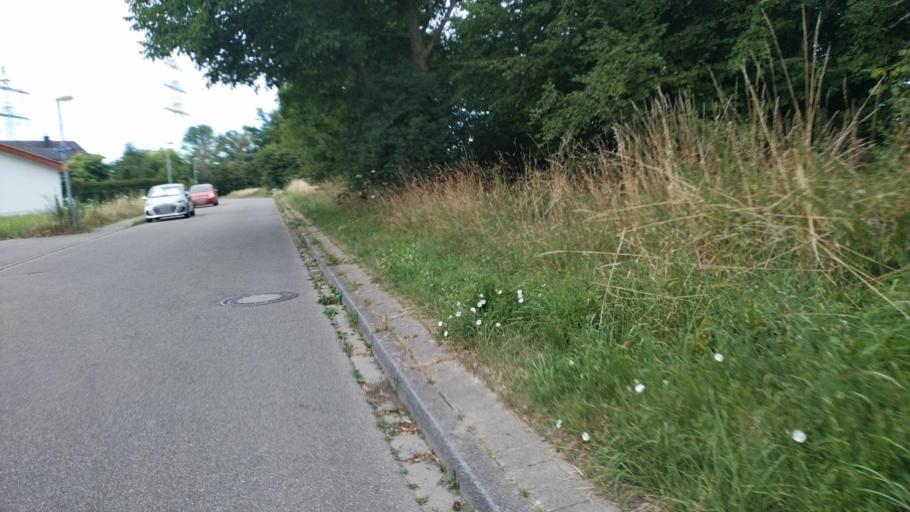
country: DE
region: Baden-Wuerttemberg
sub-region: Karlsruhe Region
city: Ettlingen
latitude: 48.9645
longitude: 8.3953
